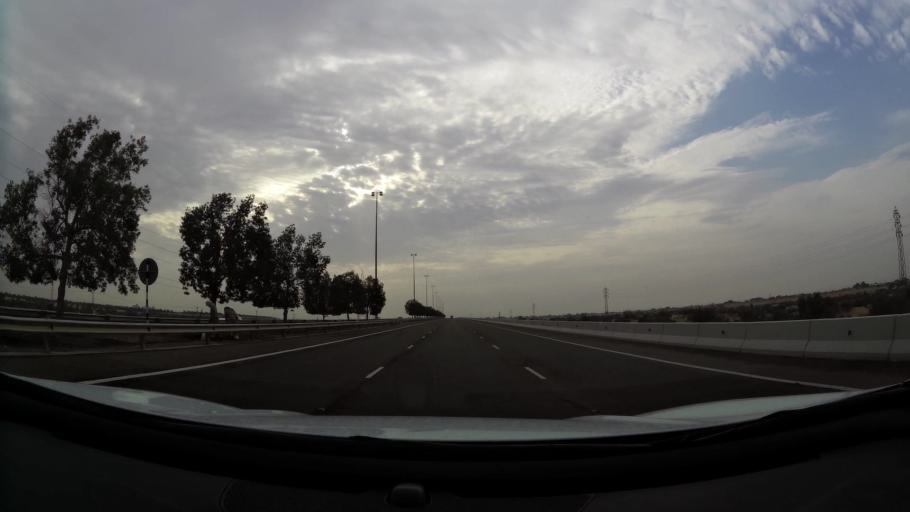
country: AE
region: Abu Dhabi
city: Abu Dhabi
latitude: 24.2090
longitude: 54.8934
